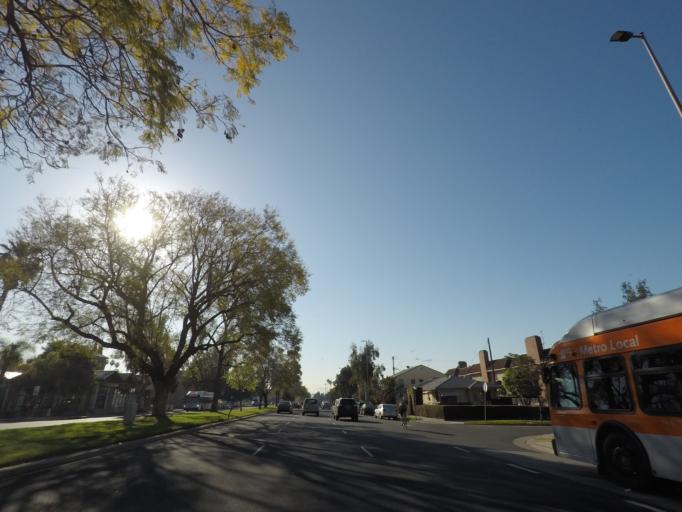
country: US
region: California
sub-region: Los Angeles County
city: Burbank
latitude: 34.1727
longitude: -118.2920
